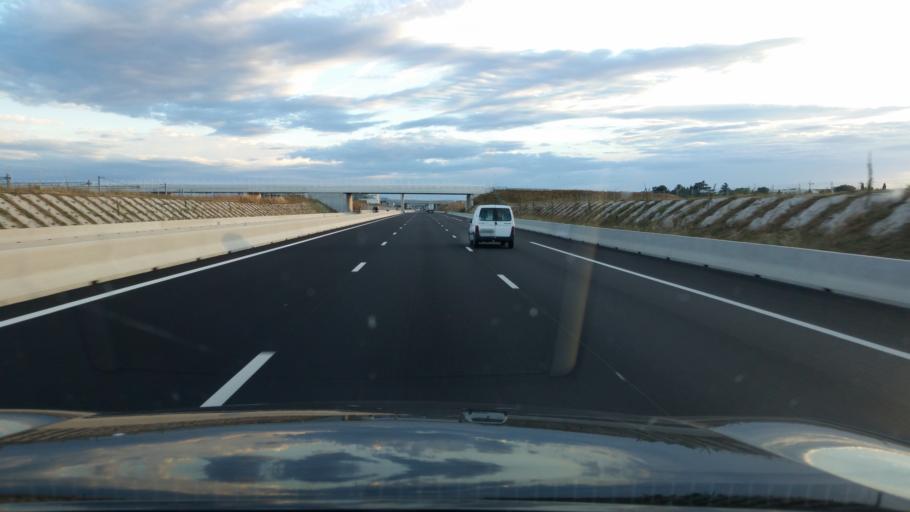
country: FR
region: Languedoc-Roussillon
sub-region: Departement de l'Herault
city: Lattes
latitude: 43.5989
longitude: 3.9305
